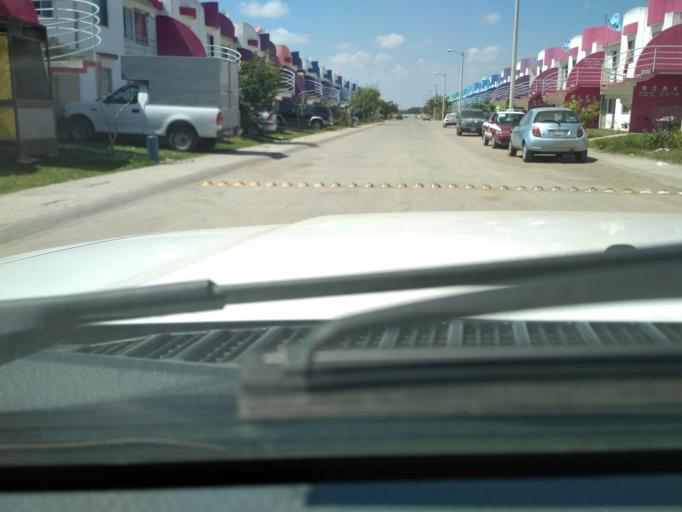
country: MX
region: Veracruz
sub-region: Veracruz
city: Las Amapolas
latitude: 19.1341
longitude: -96.2068
